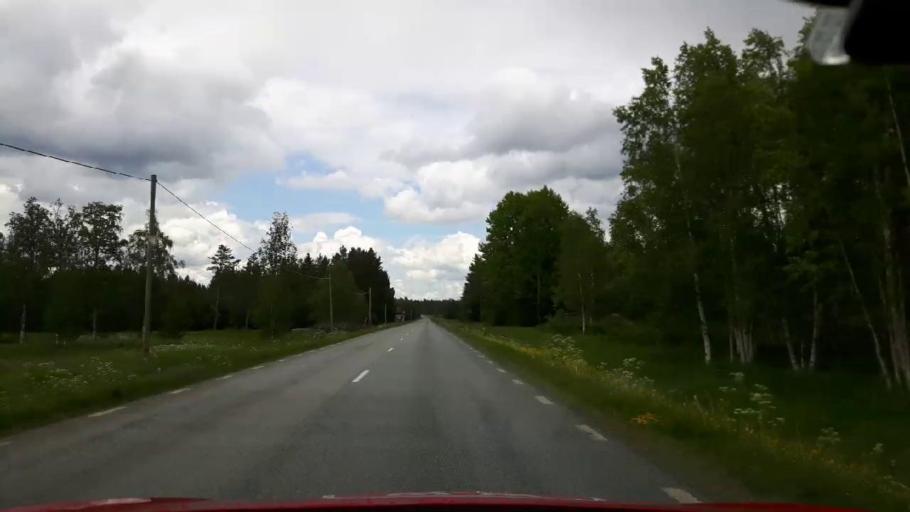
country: SE
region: Jaemtland
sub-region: Krokoms Kommun
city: Krokom
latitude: 63.5085
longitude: 14.2214
